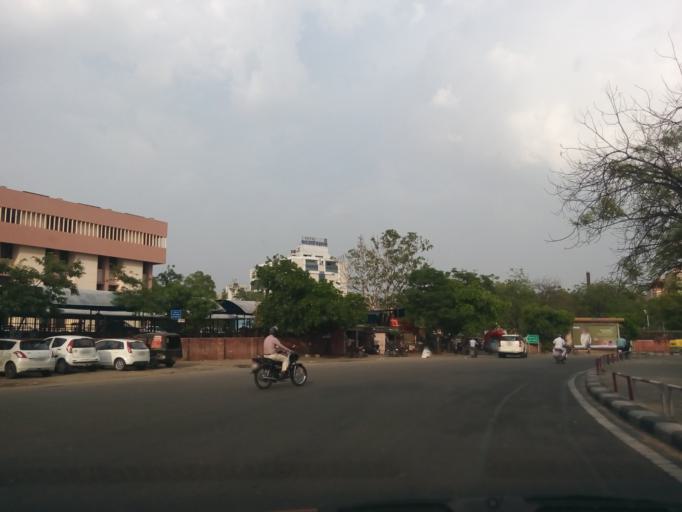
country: IN
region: Rajasthan
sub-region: Jaipur
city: Jaipur
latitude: 26.9267
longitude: 75.7929
